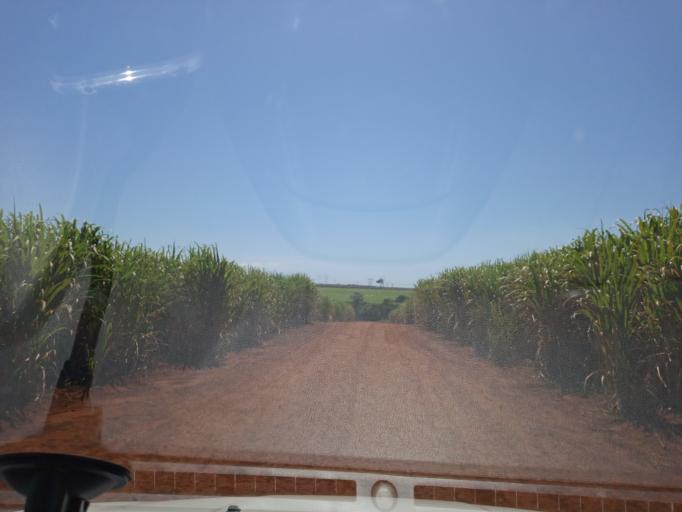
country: BR
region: Goias
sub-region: Itumbiara
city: Itumbiara
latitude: -18.4418
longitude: -49.1469
